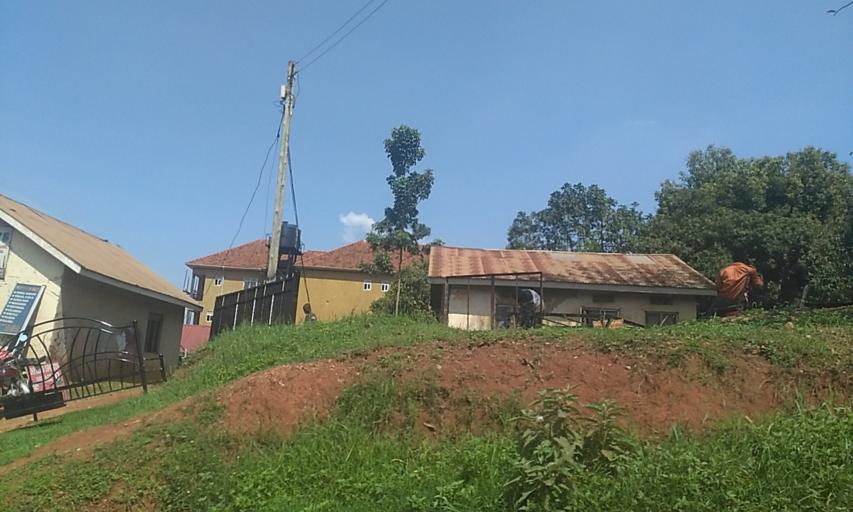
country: UG
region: Central Region
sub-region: Wakiso District
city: Kireka
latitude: 0.3730
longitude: 32.6014
